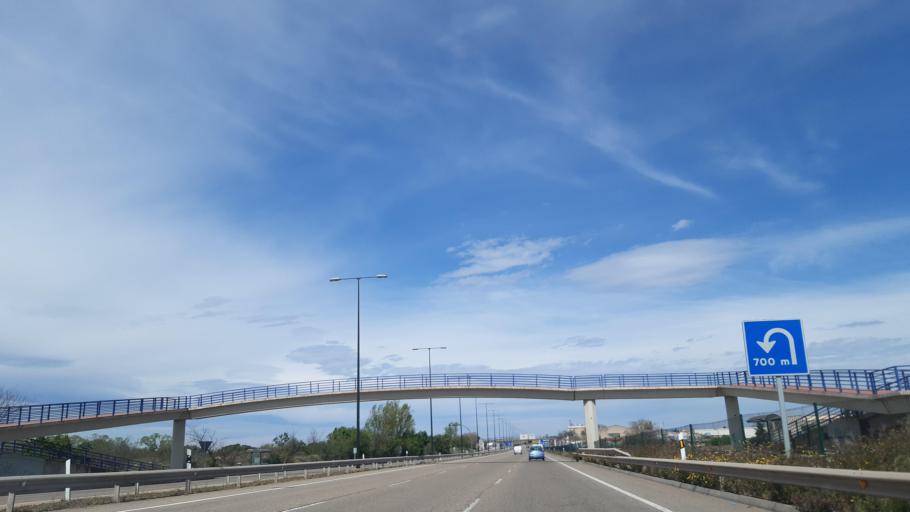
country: ES
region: Aragon
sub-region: Provincia de Zaragoza
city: Utebo
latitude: 41.6913
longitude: -0.9827
